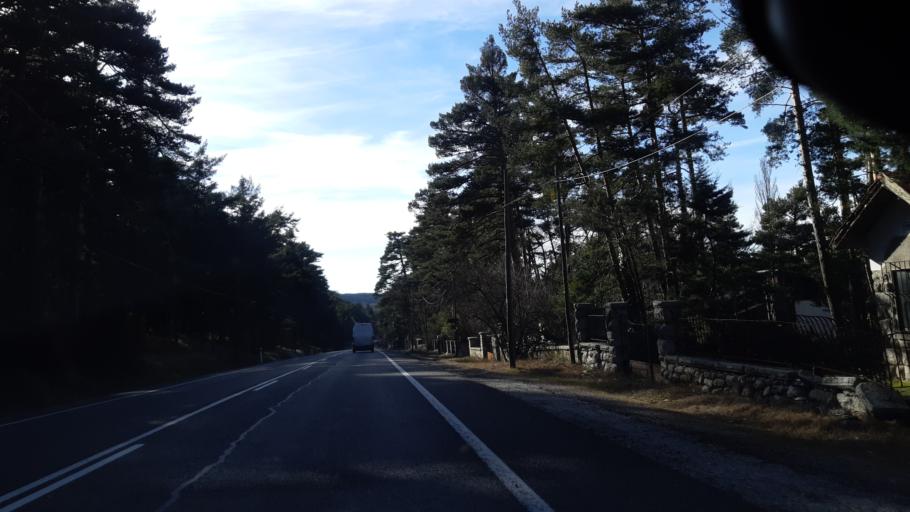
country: ES
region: Madrid
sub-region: Provincia de Madrid
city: Guadarrama
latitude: 40.7107
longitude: -4.1709
